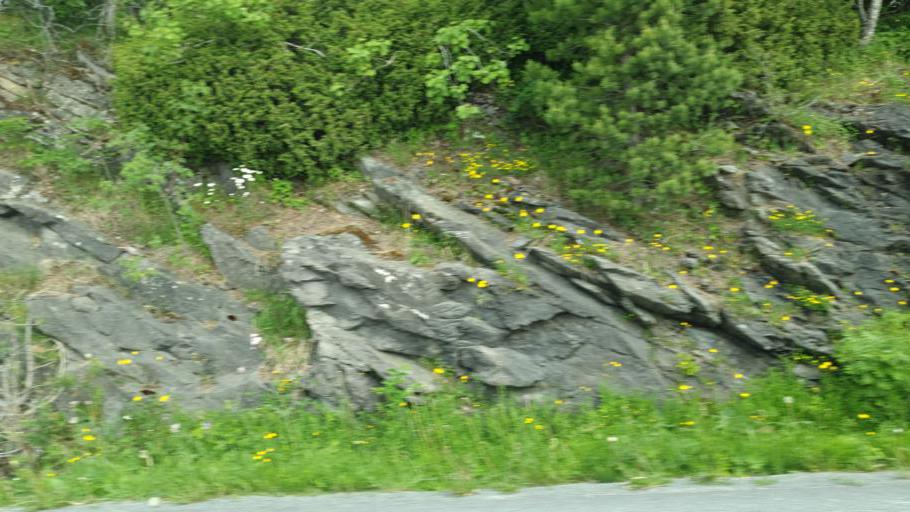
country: NO
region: Sor-Trondelag
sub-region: Trondheim
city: Trondheim
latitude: 63.5570
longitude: 10.2821
